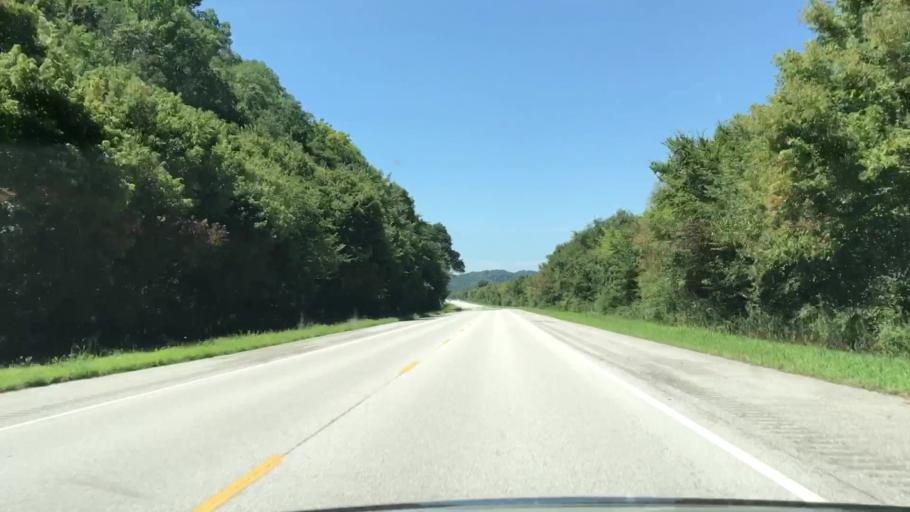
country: US
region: Tennessee
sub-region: Jackson County
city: Gainesboro
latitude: 36.4387
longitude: -85.6015
